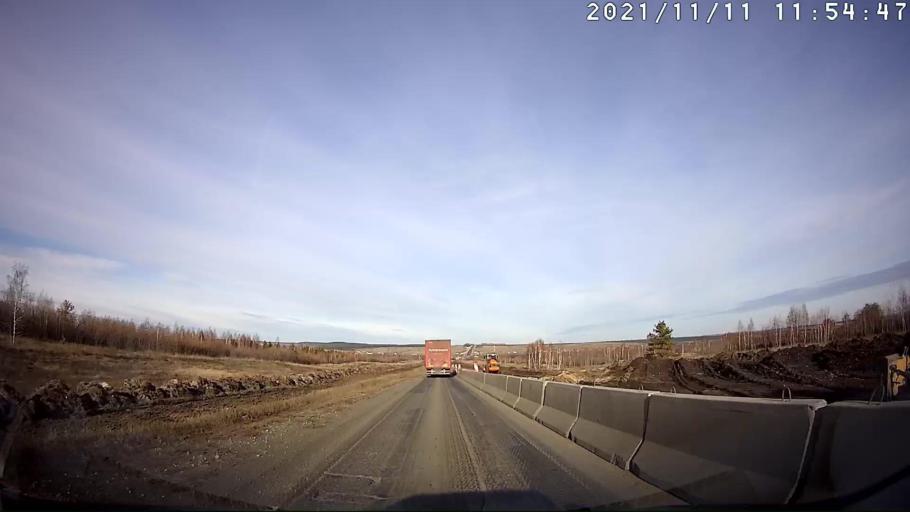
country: RU
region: Samara
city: Varlamovo
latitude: 53.5337
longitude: 48.3387
